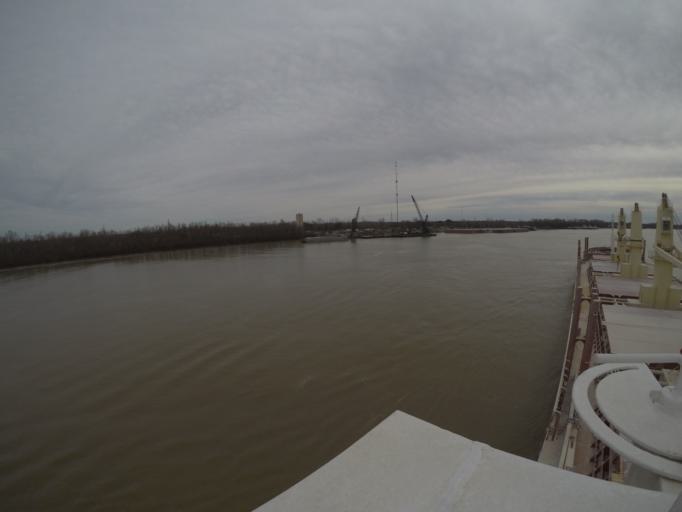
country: US
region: Louisiana
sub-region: Saint John the Baptist Parish
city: Laplace
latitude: 30.0500
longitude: -90.4813
